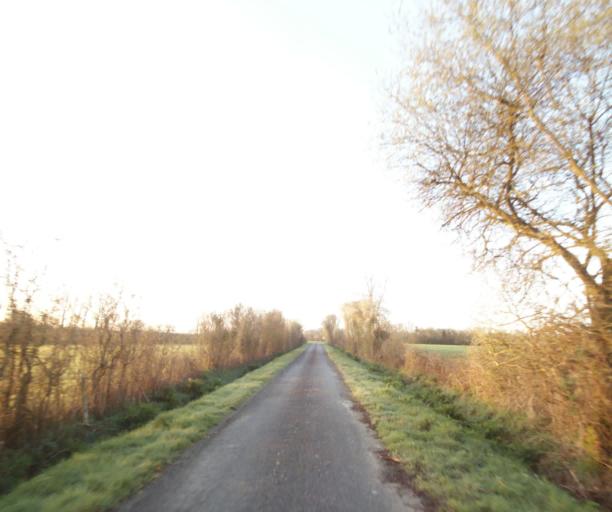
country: FR
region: Pays de la Loire
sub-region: Departement de la Loire-Atlantique
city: Quilly
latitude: 47.4418
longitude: -1.9048
